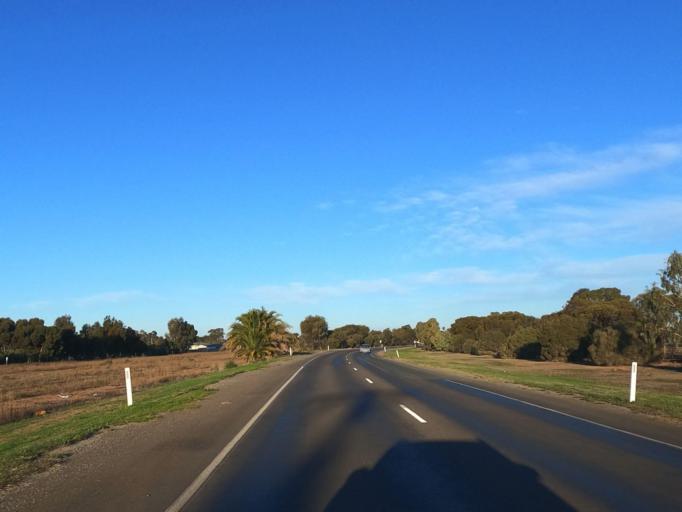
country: AU
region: Victoria
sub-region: Swan Hill
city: Swan Hill
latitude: -35.3371
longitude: 143.5369
